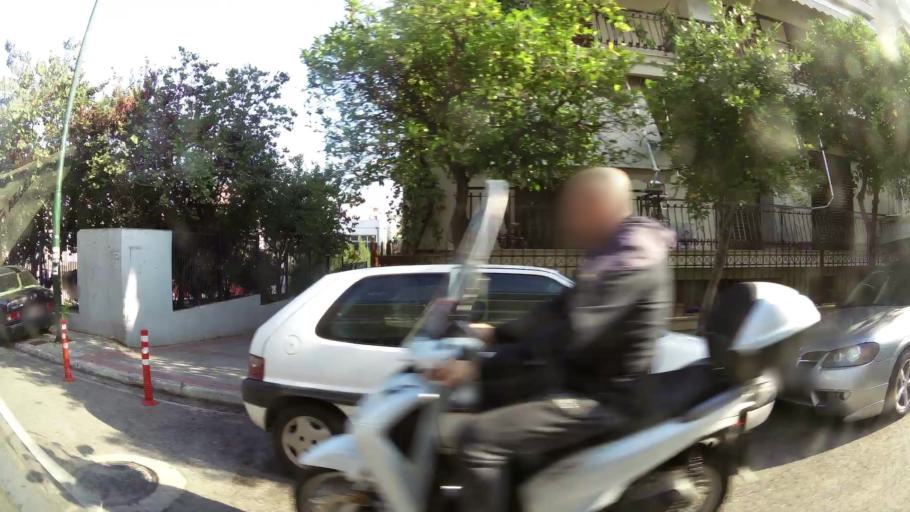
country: GR
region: Attica
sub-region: Nomarchia Athinas
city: Kaisariani
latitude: 37.9709
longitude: 23.7744
